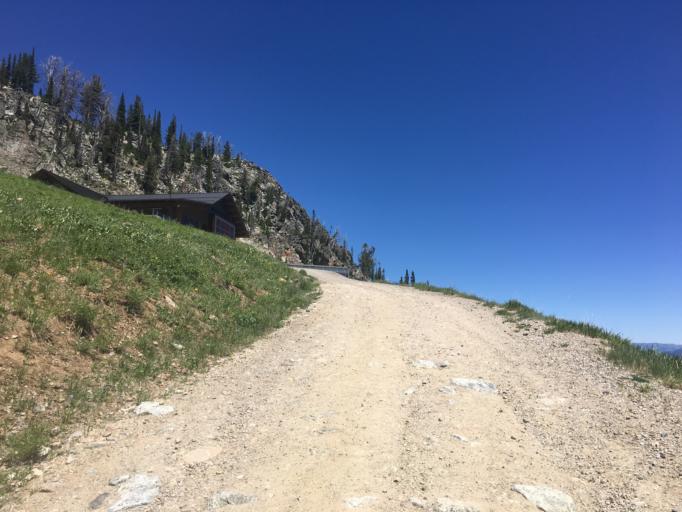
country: US
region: Wyoming
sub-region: Teton County
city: Moose Wilson Road
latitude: 43.6009
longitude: -110.8548
